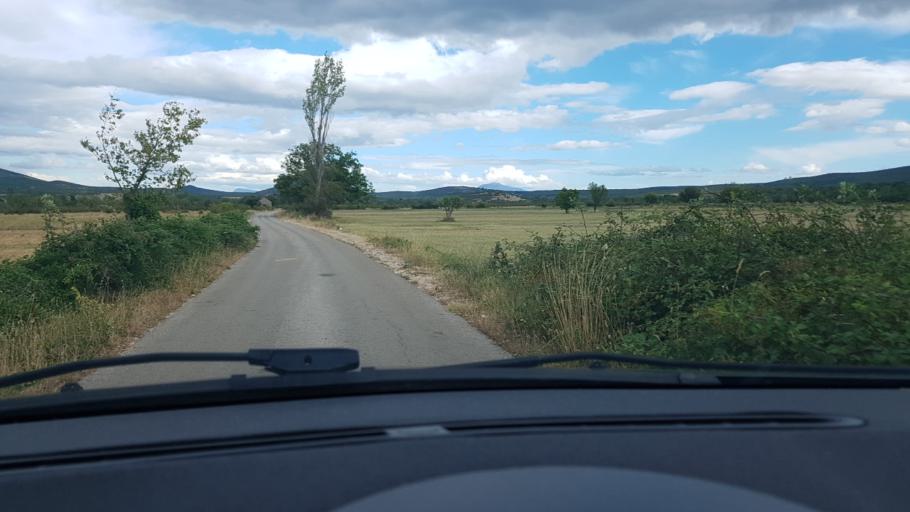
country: HR
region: Sibensko-Kniniska
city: Kistanje
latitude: 44.1094
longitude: 15.9275
